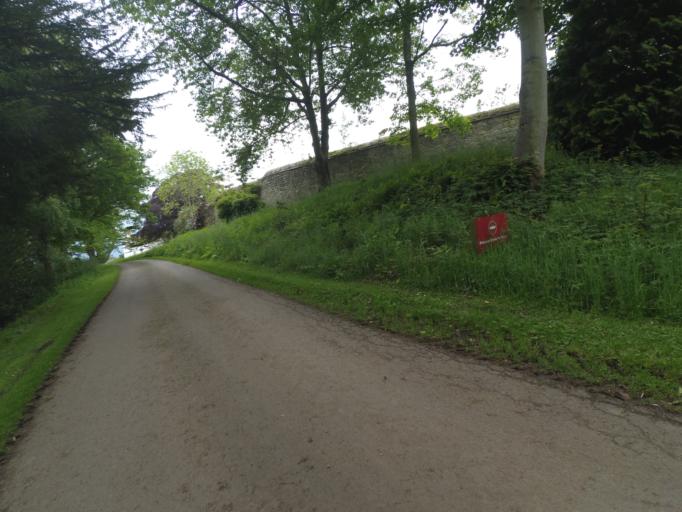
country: GB
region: Scotland
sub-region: East Lothian
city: Pencaitland
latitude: 55.9162
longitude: -2.8983
